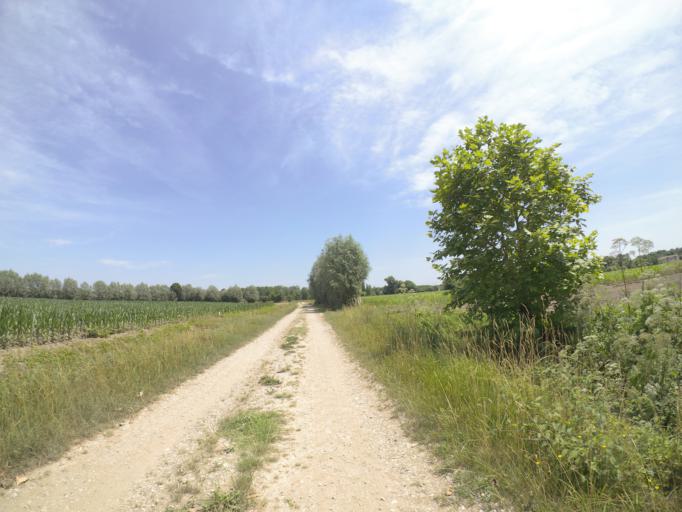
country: IT
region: Friuli Venezia Giulia
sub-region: Provincia di Udine
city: Camino al Tagliamento
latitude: 45.9036
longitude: 12.9569
